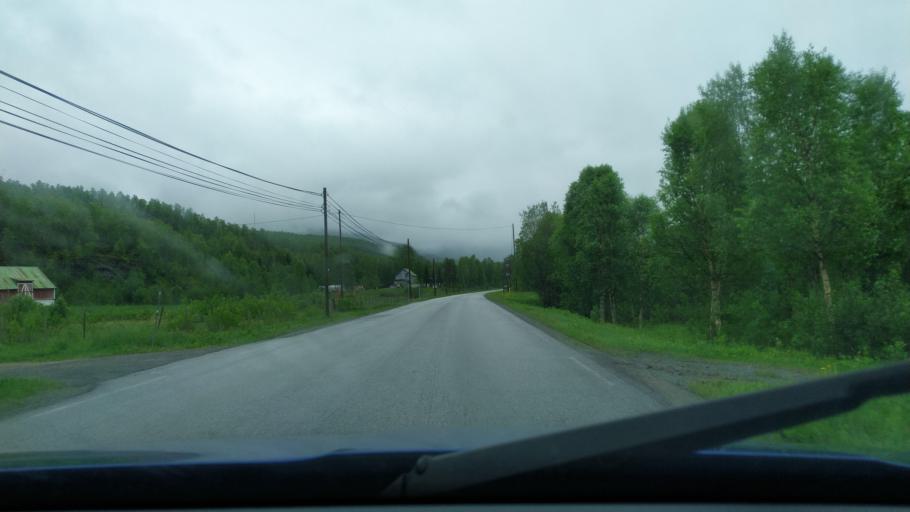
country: NO
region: Troms
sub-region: Dyroy
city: Brostadbotn
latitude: 69.0705
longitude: 17.7342
